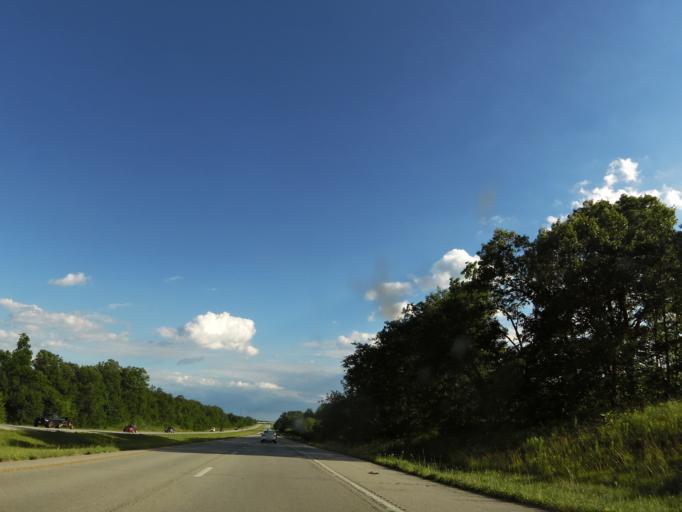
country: US
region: Missouri
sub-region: Lincoln County
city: Troy
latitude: 39.0635
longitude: -90.9740
